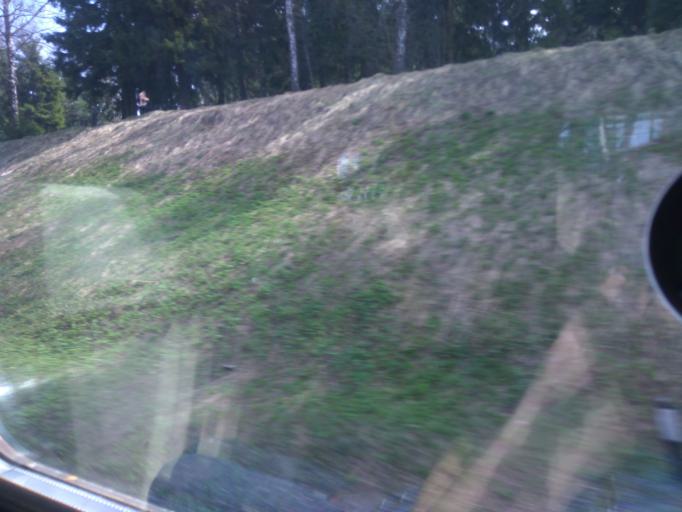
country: RU
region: Moskovskaya
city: Lugovaya
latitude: 56.0596
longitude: 37.4869
